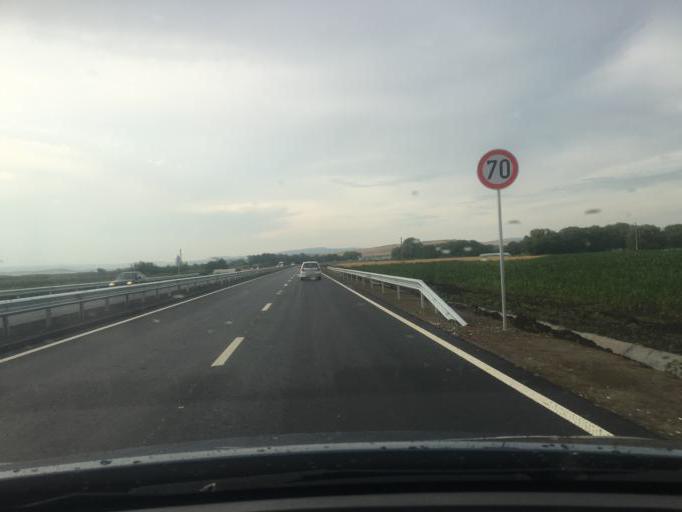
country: BG
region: Burgas
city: Aheloy
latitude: 42.6472
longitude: 27.6369
